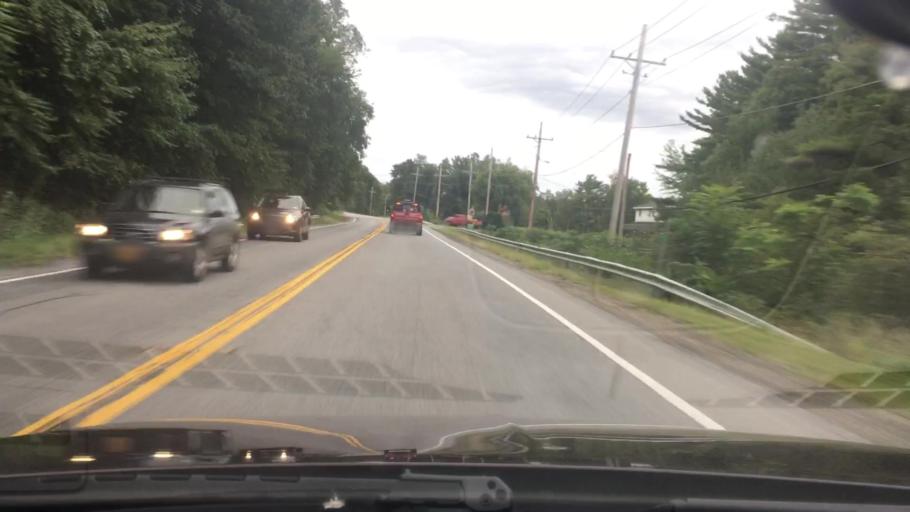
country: US
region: New York
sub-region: Dutchess County
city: Pleasant Valley
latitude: 41.7706
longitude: -73.7740
